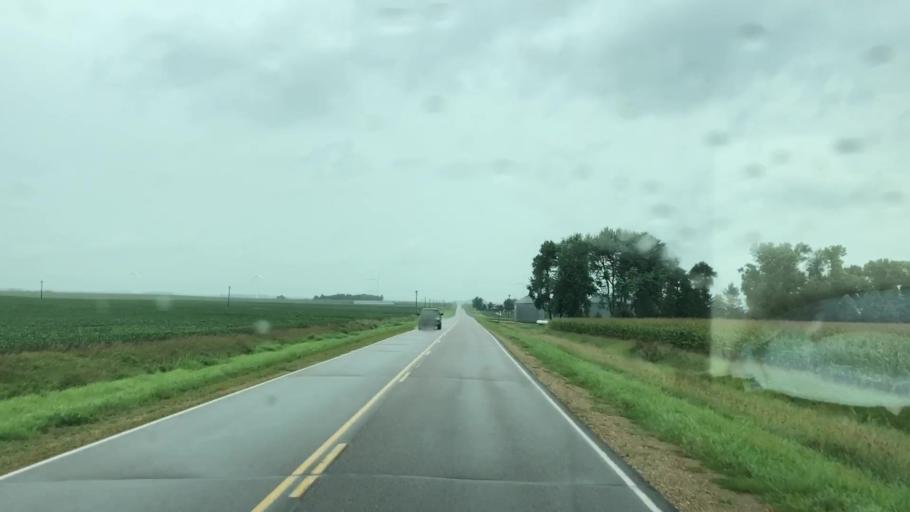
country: US
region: Iowa
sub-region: O'Brien County
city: Sanborn
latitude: 43.2180
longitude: -95.7234
